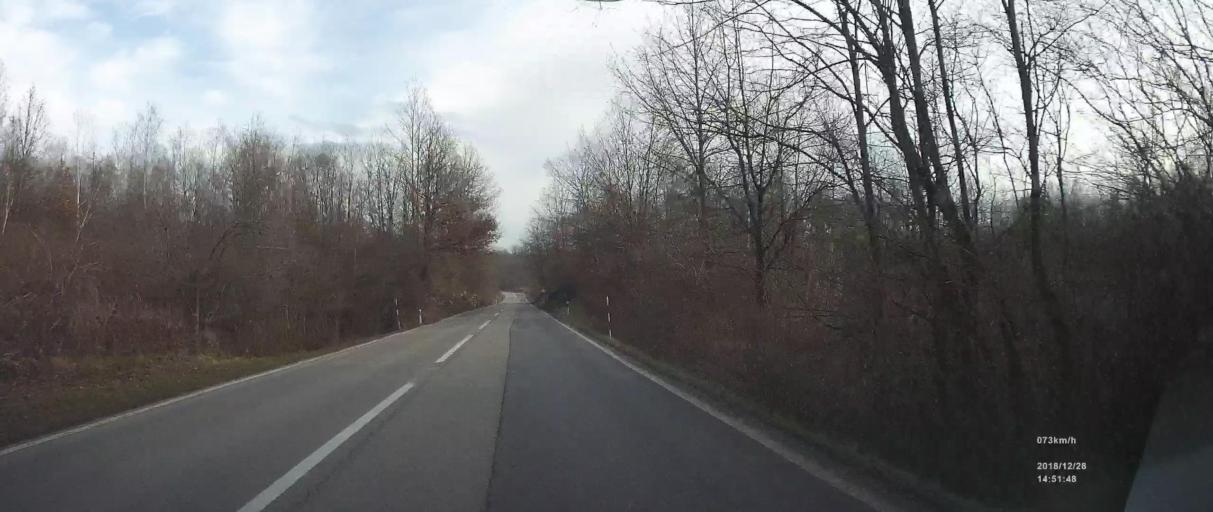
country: HR
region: Karlovacka
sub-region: Grad Karlovac
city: Karlovac
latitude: 45.4463
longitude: 15.3877
